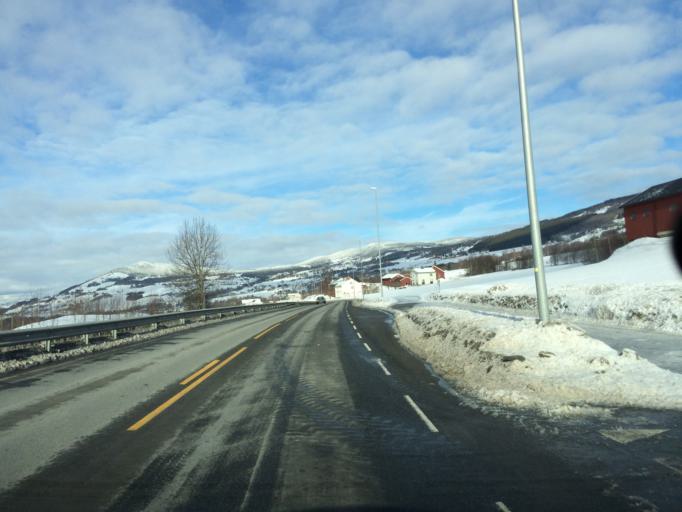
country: NO
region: Oppland
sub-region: Gausdal
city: Segalstad bru
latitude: 61.1968
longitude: 10.3095
